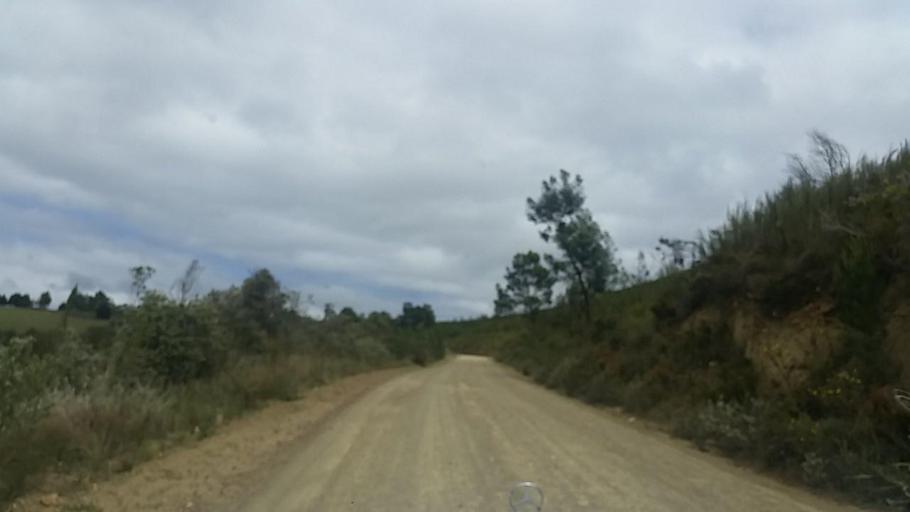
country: ZA
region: Western Cape
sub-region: Eden District Municipality
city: Knysna
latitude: -33.7556
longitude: 23.1663
